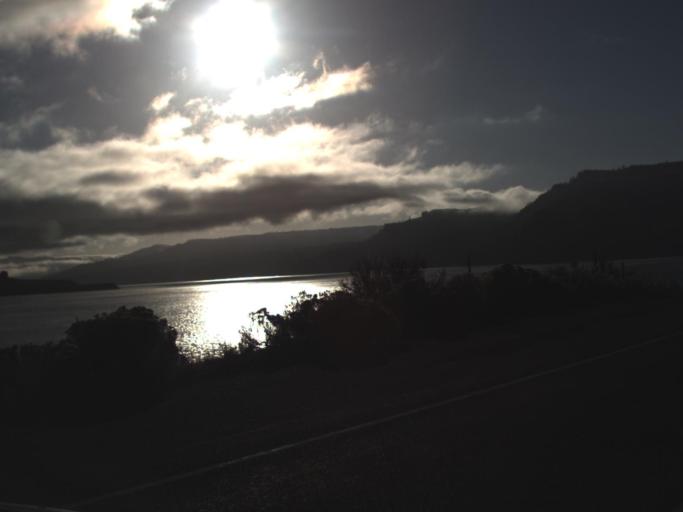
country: US
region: Washington
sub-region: Okanogan County
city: Coulee Dam
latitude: 47.9529
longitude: -118.6915
